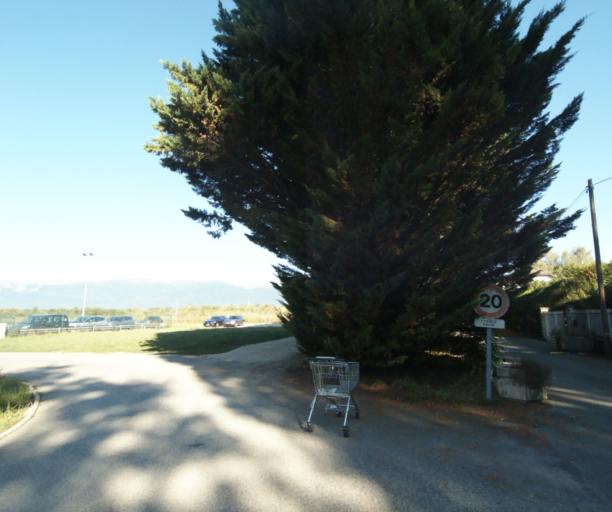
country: FR
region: Rhone-Alpes
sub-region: Departement de l'Ain
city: Ferney-Voltaire
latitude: 46.2472
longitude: 6.0949
